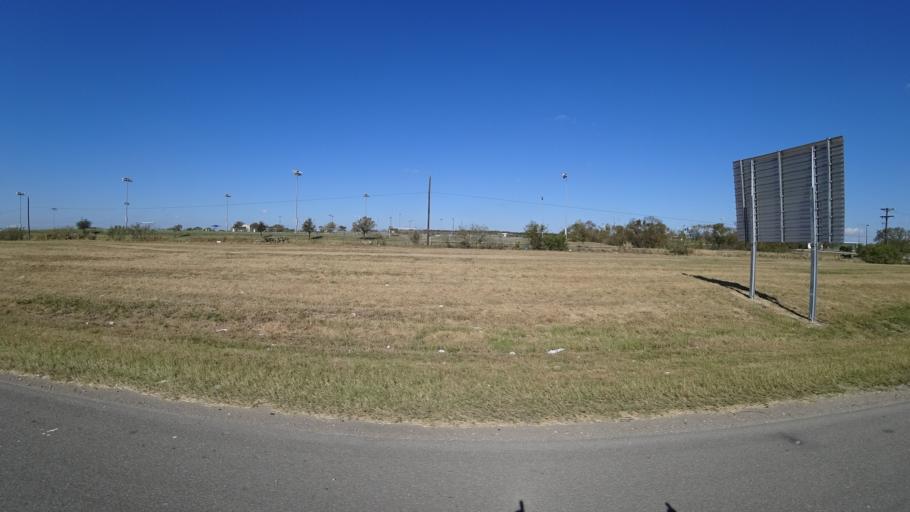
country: US
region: Texas
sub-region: Travis County
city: Garfield
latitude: 30.1864
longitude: -97.6105
